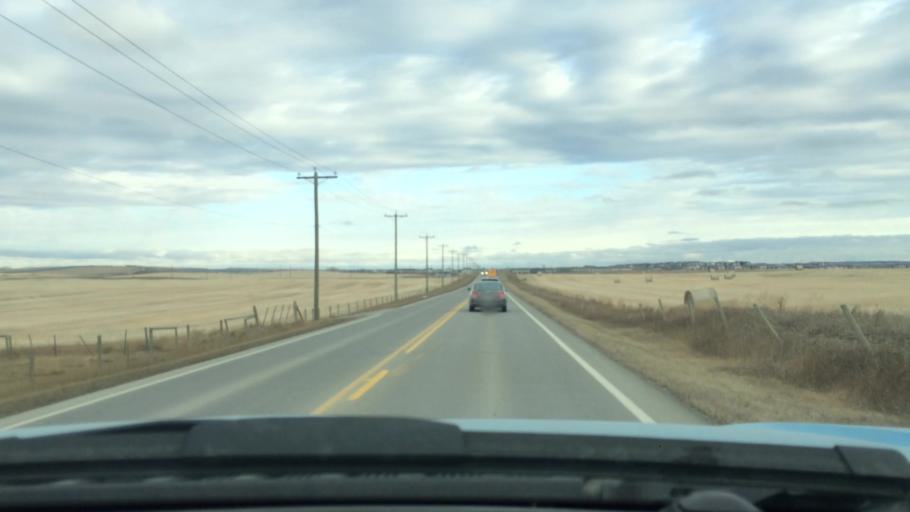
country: CA
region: Alberta
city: Airdrie
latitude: 51.2346
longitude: -114.0249
